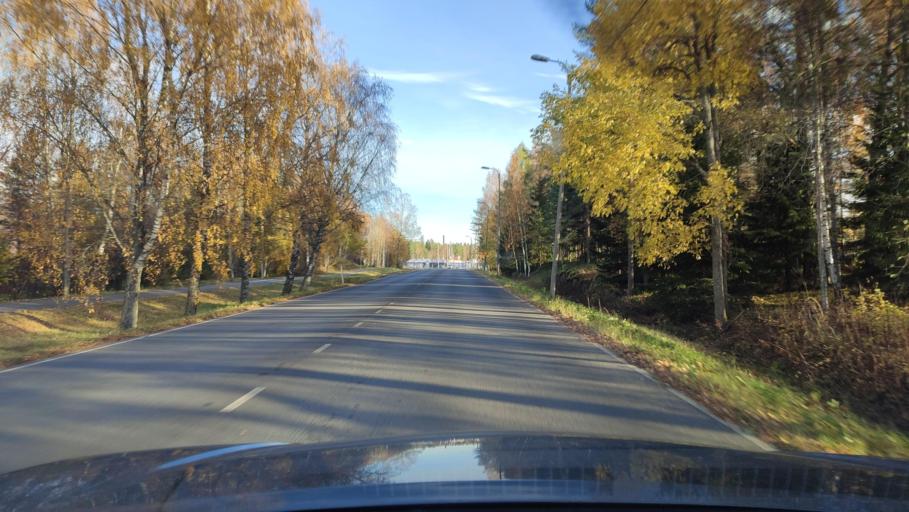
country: FI
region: Ostrobothnia
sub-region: Vaasa
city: Vaasa
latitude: 63.0802
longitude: 21.6539
